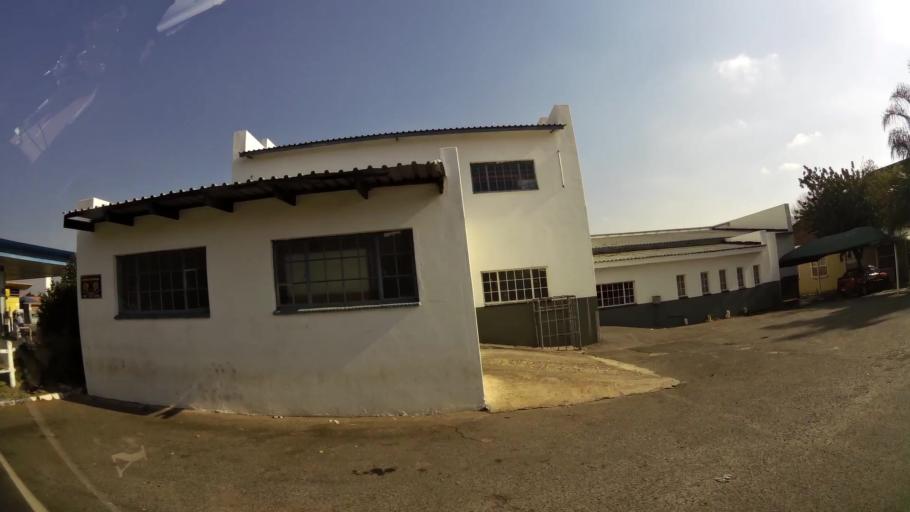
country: ZA
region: Gauteng
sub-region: West Rand District Municipality
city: Randfontein
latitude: -26.1670
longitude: 27.6983
